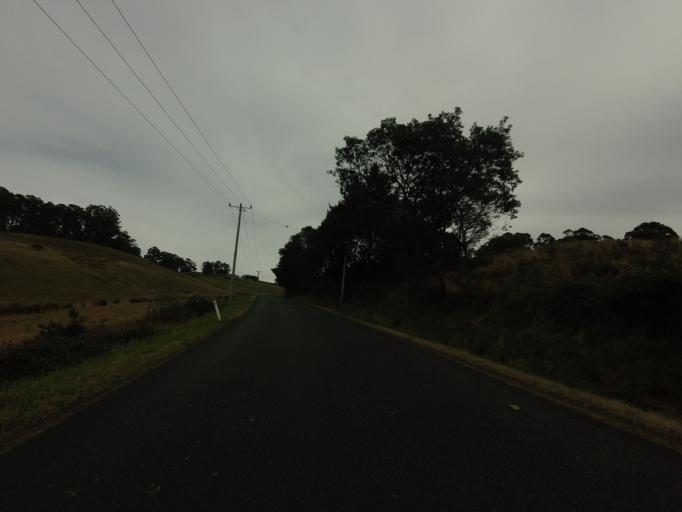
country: AU
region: Tasmania
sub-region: Sorell
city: Sorell
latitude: -42.5345
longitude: 147.5676
